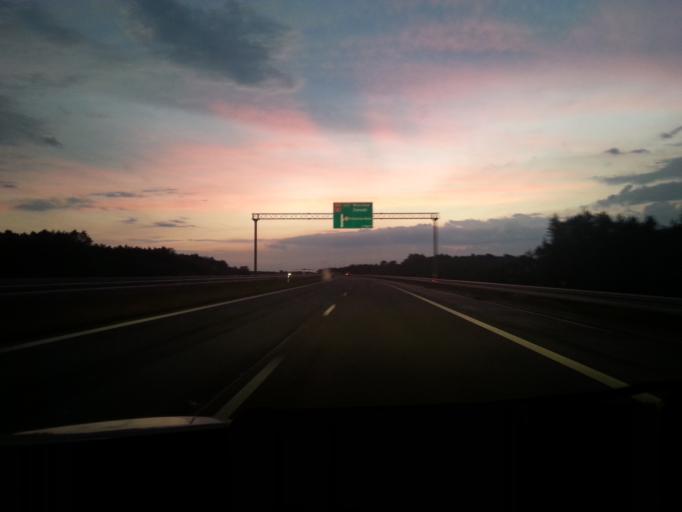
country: PL
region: Lodz Voivodeship
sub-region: Powiat zdunskowolski
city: Zapolice
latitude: 51.5931
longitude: 18.8875
